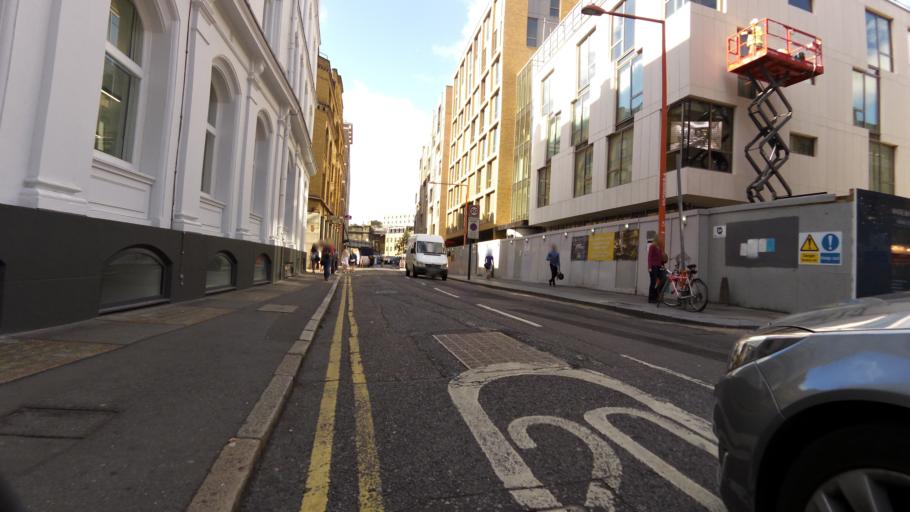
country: GB
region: England
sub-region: Greater London
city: City of London
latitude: 51.5058
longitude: -0.1008
